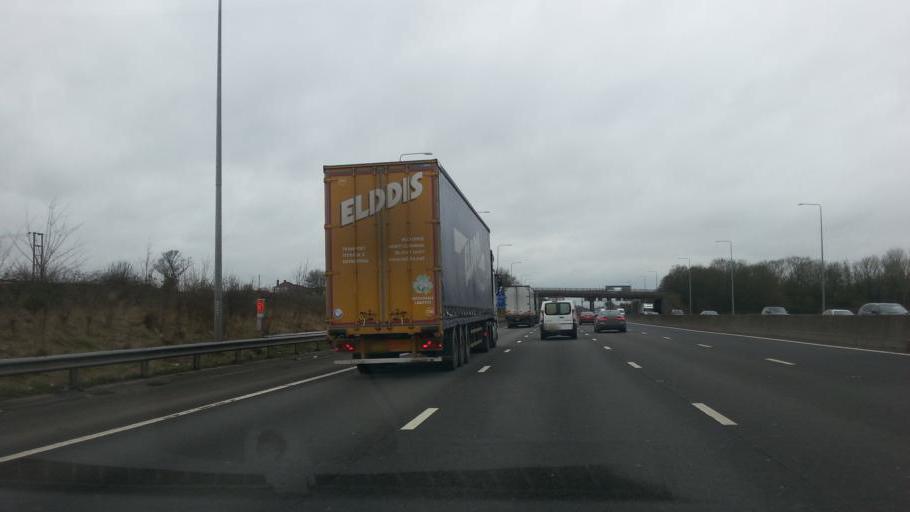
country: GB
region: England
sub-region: Derbyshire
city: Pinxton
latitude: 53.0713
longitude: -1.2805
